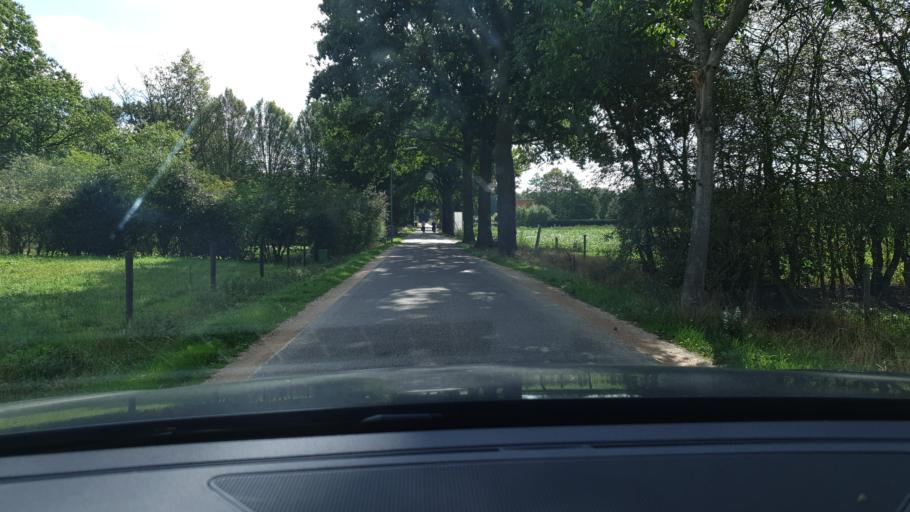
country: NL
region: Gelderland
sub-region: Gemeente Groesbeek
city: De Horst
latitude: 51.7694
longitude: 5.9863
